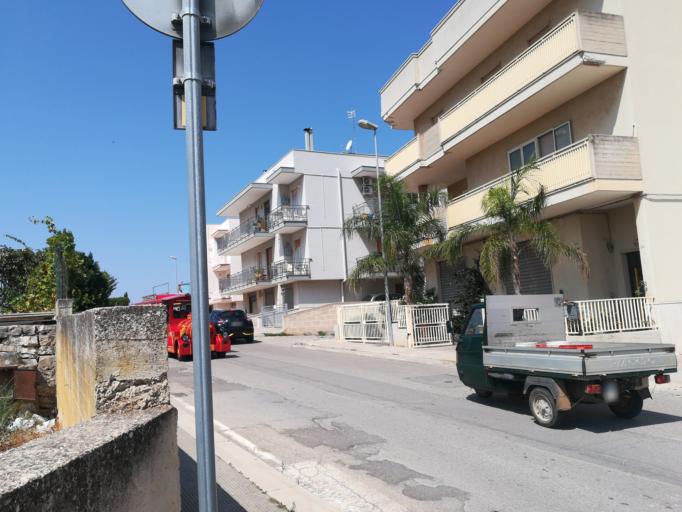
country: IT
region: Apulia
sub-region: Provincia di Bari
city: Polignano a Mare
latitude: 40.9948
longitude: 17.2148
